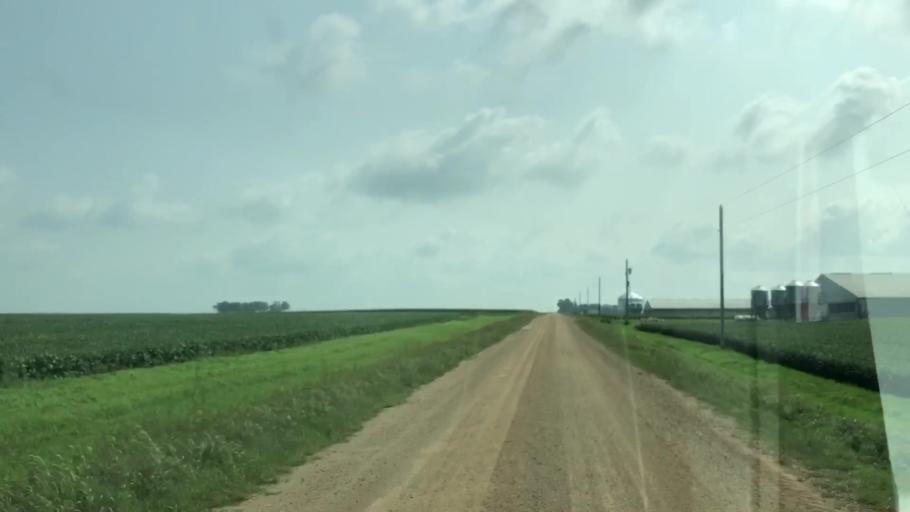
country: US
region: Iowa
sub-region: O'Brien County
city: Sheldon
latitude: 43.2153
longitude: -95.9574
